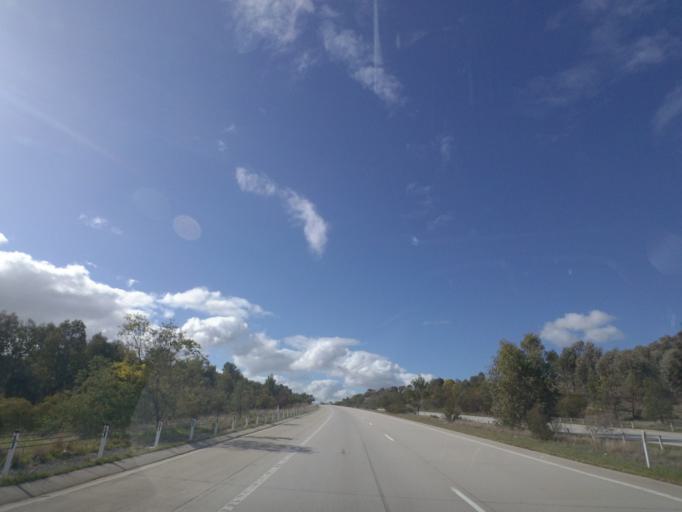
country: AU
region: New South Wales
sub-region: Albury Municipality
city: Lavington
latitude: -35.9230
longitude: 147.0925
